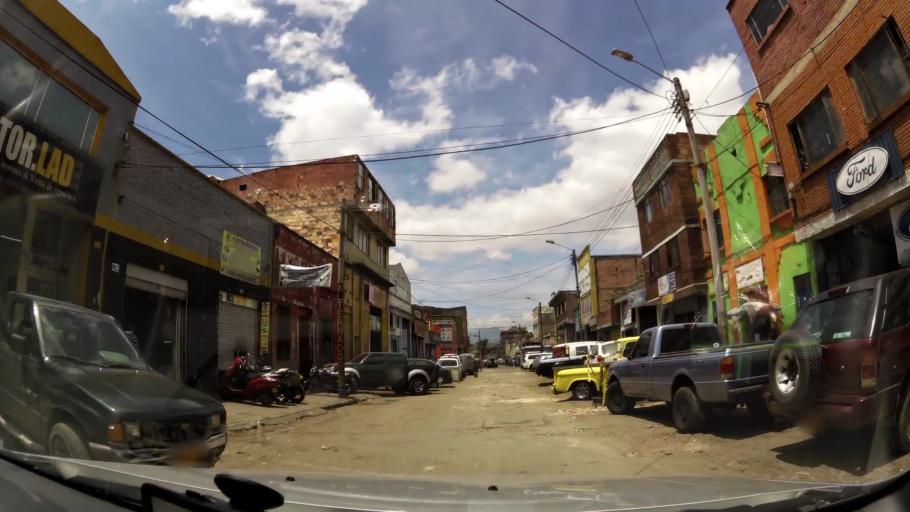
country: CO
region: Bogota D.C.
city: Bogota
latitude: 4.6007
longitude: -74.0842
